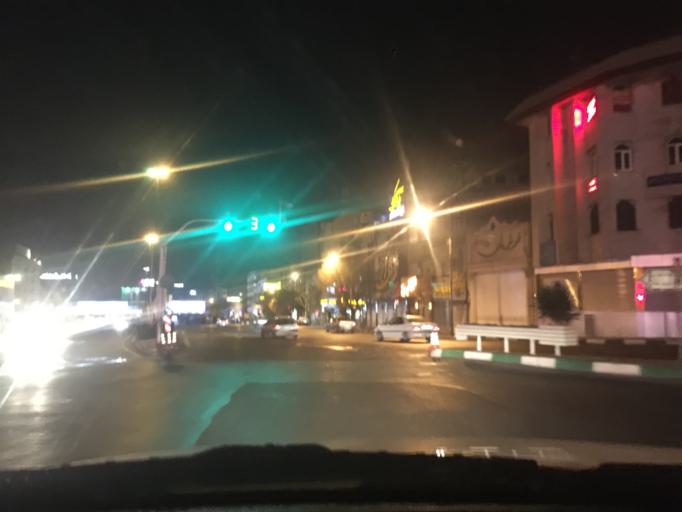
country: IR
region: Tehran
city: Tehran
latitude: 35.7191
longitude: 51.4277
